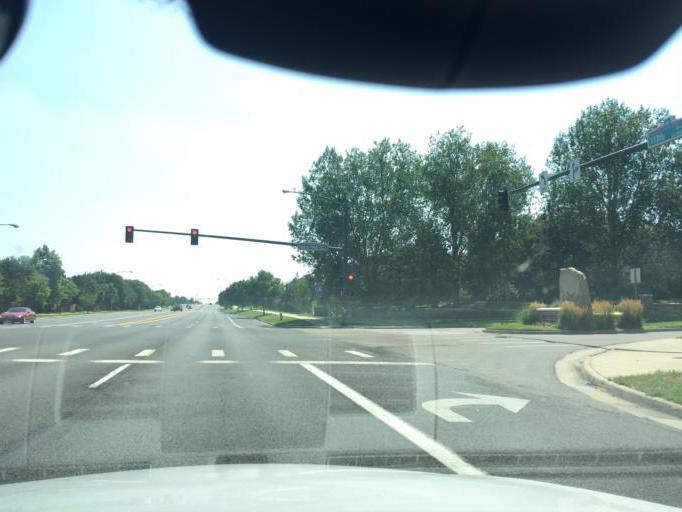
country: US
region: Colorado
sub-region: Adams County
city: Northglenn
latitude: 39.8996
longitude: -105.0327
